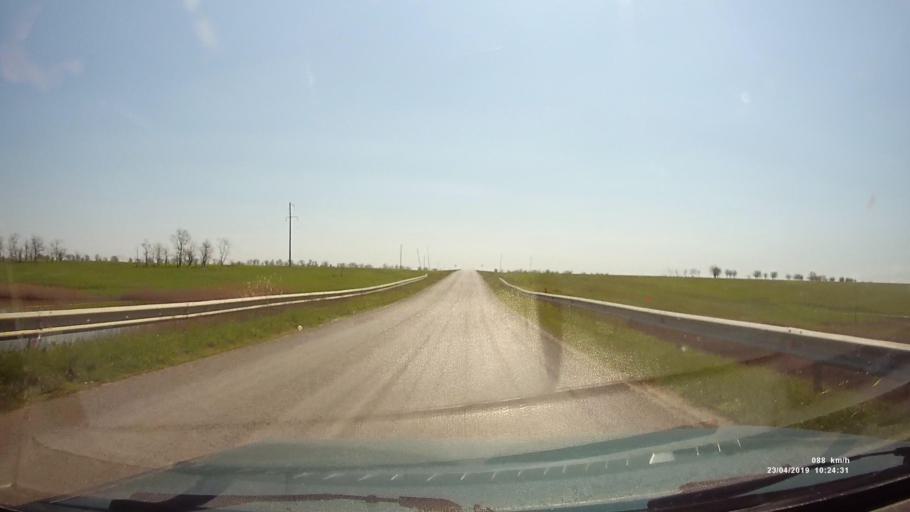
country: RU
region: Rostov
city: Sovetskoye
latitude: 46.6382
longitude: 42.4429
